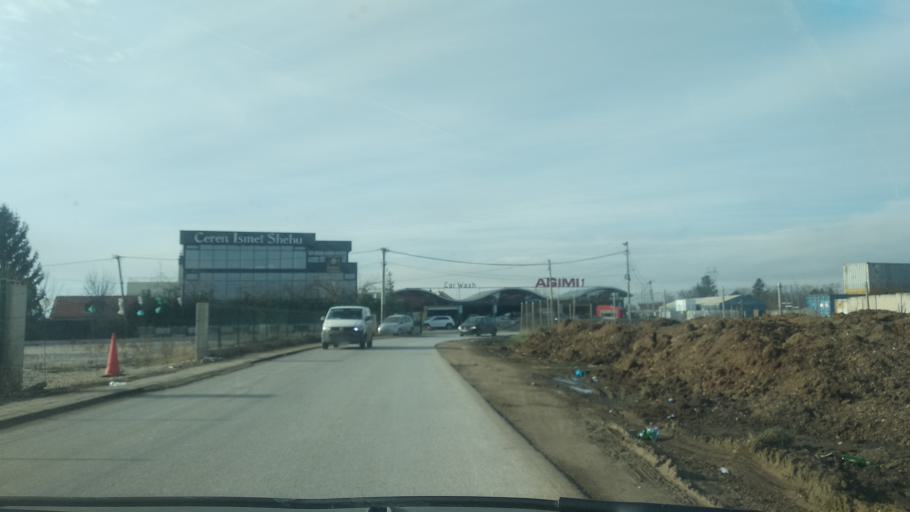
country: XK
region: Pristina
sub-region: Lipjan
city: Lipljan
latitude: 42.5943
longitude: 21.1292
